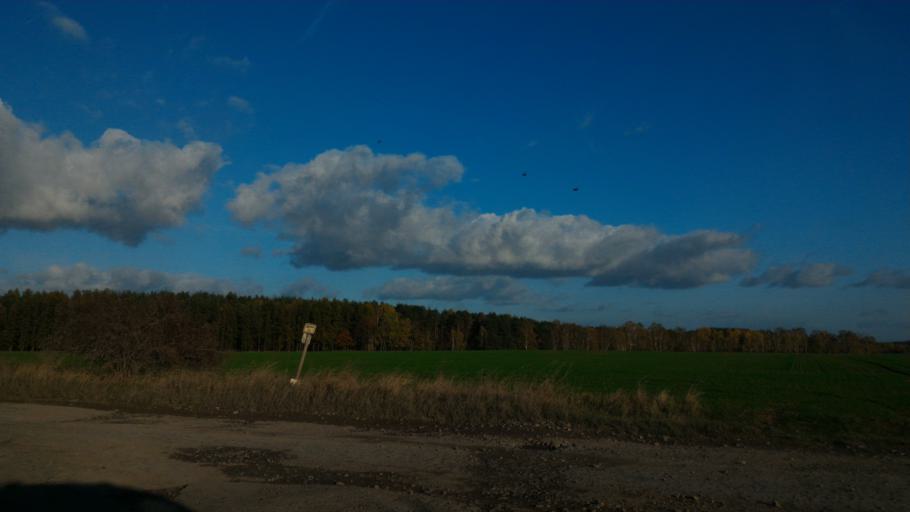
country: CZ
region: Central Bohemia
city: Bela pod Bezdezem
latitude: 50.5218
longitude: 14.7558
